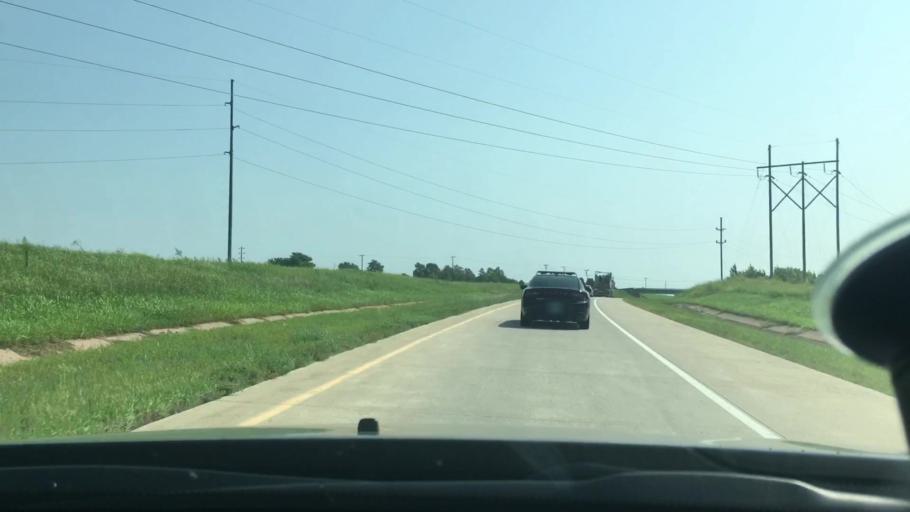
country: US
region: Oklahoma
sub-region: Pontotoc County
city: Ada
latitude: 34.7883
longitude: -96.6918
